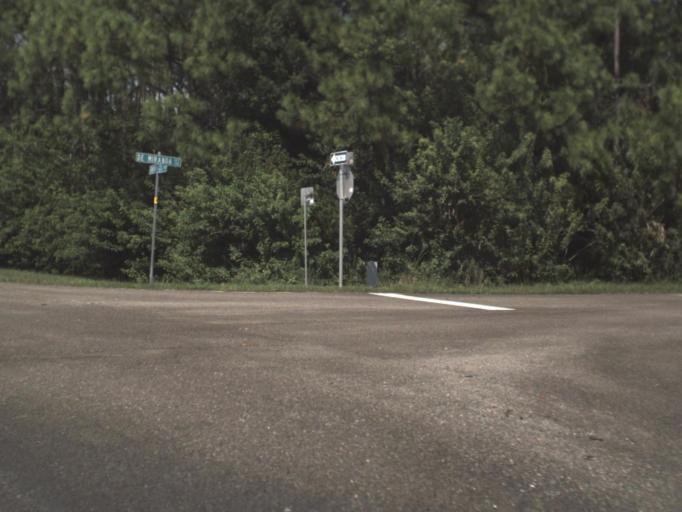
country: US
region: Florida
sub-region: Sarasota County
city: Warm Mineral Springs
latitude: 27.0484
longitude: -82.2814
